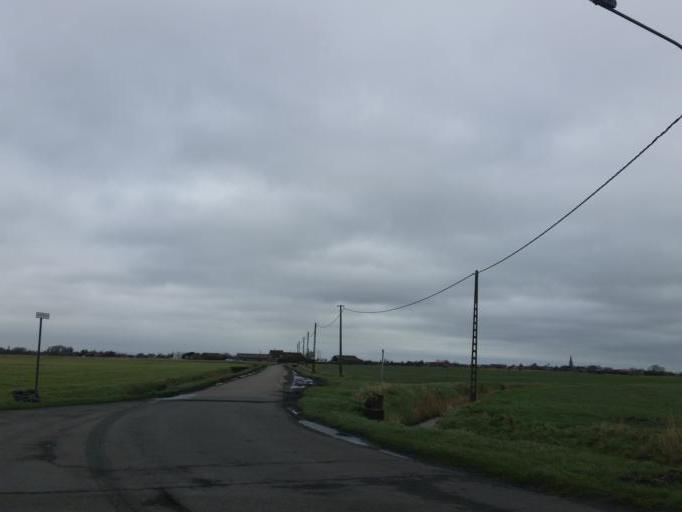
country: BE
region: Flanders
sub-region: Provincie West-Vlaanderen
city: Bredene
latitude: 51.2366
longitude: 2.9977
